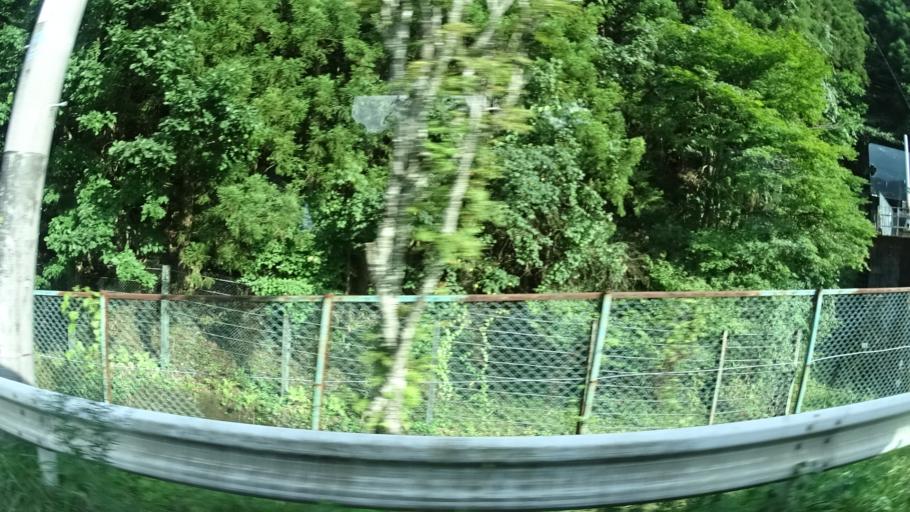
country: JP
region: Tochigi
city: Nikko
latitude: 36.7263
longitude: 139.5455
